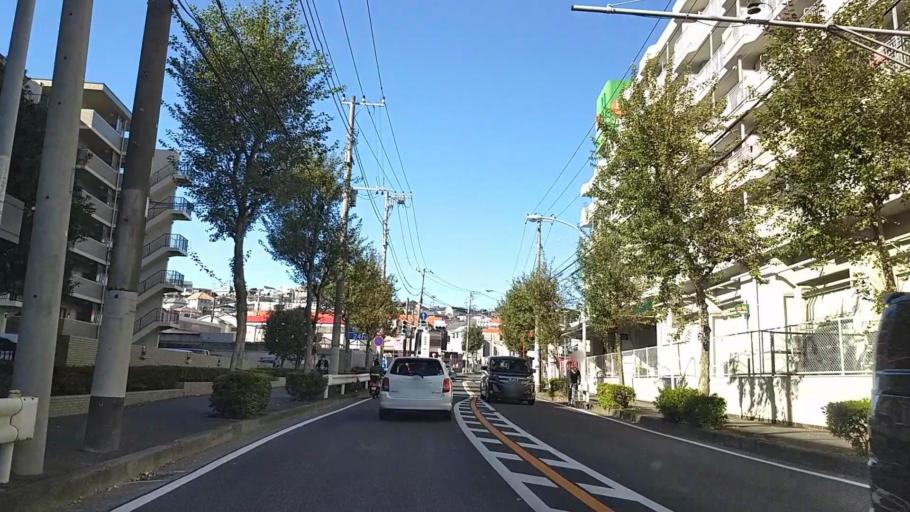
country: JP
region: Kanagawa
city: Yokohama
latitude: 35.4231
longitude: 139.5864
